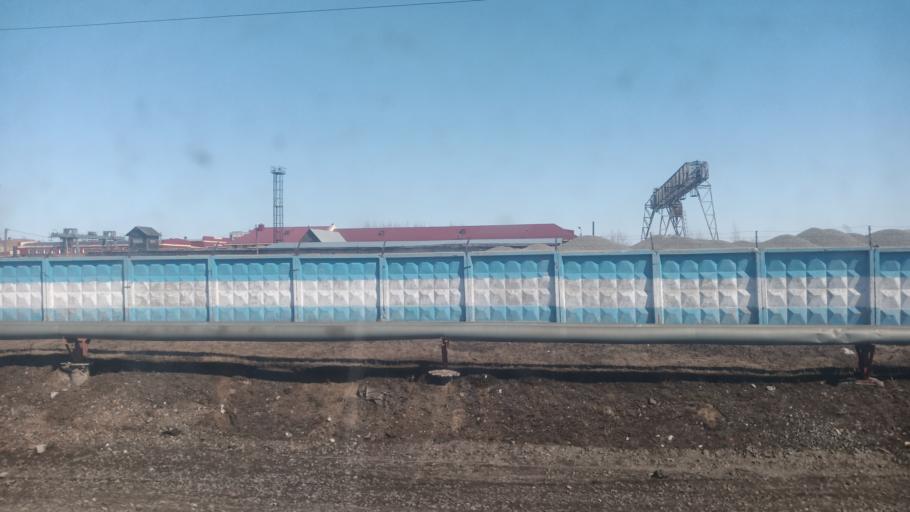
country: RU
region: Altai Krai
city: Novoaltaysk
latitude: 53.4134
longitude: 83.9208
